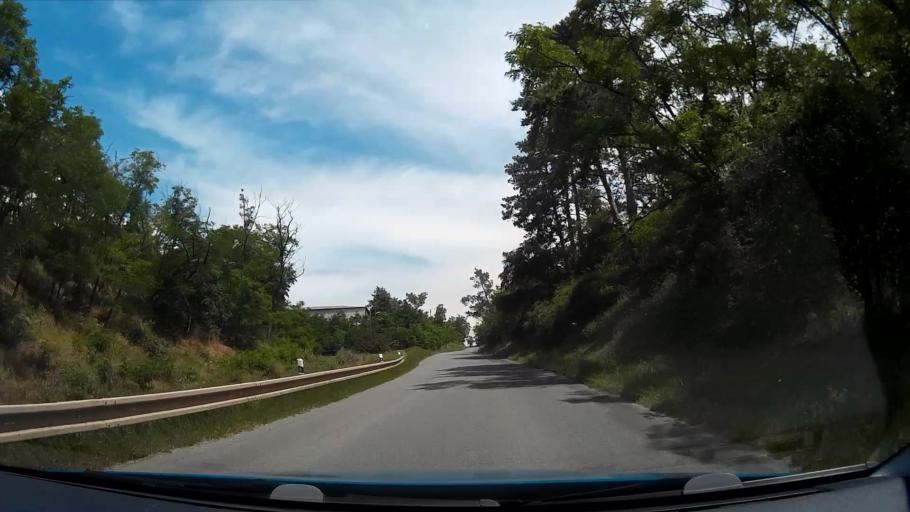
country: CZ
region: South Moravian
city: Dolni Kounice
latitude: 49.0534
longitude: 16.5039
